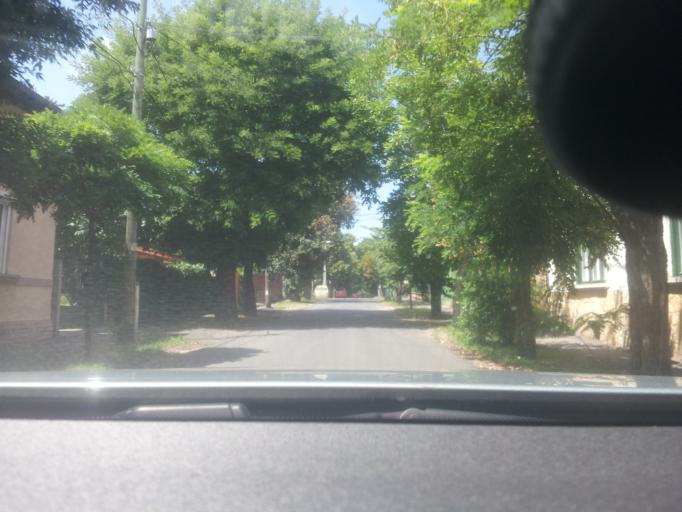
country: HU
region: Budapest
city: Budapest XVIII. keruelet
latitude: 47.4374
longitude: 19.1847
